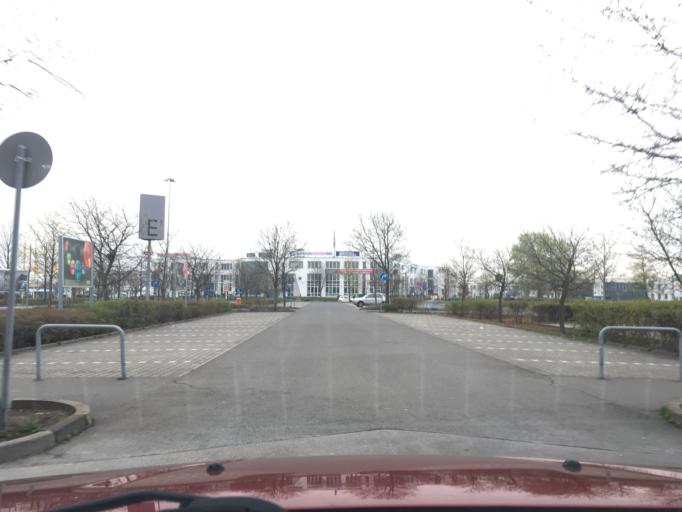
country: DE
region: Brandenburg
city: Schulzendorf
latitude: 52.3679
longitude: 13.5576
